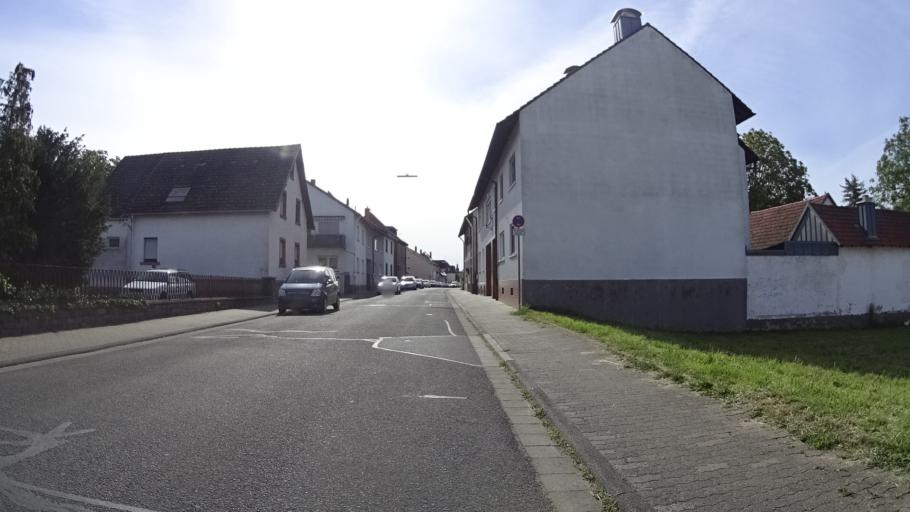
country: DE
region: Bavaria
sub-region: Regierungsbezirk Unterfranken
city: Mainaschaff
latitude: 49.9784
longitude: 9.0802
